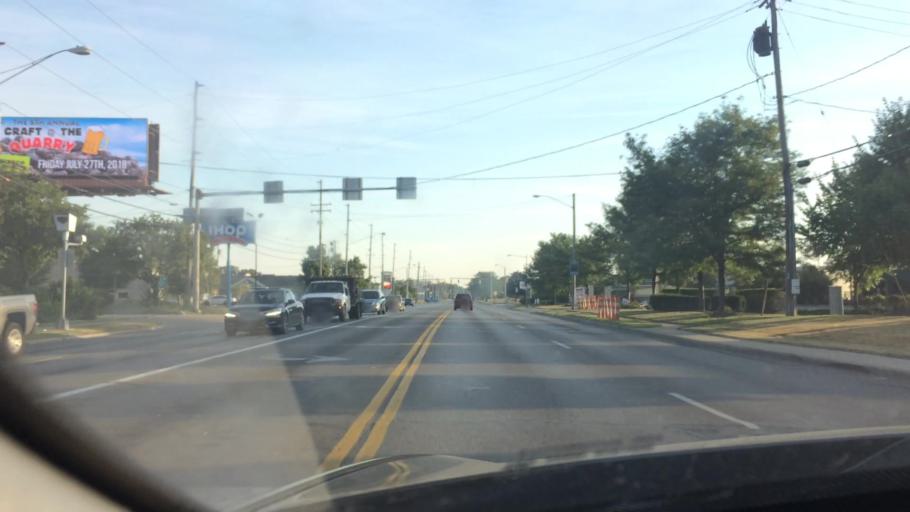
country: US
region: Ohio
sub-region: Lucas County
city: Ottawa Hills
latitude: 41.6914
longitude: -83.6446
